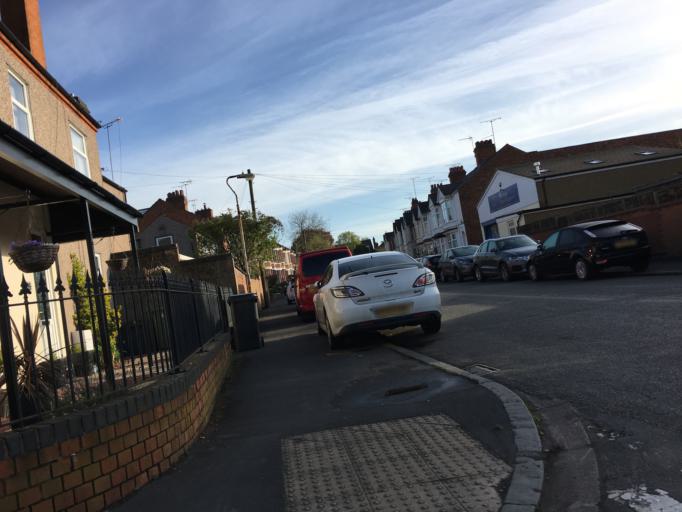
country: GB
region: England
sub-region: Warwickshire
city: Rugby
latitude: 52.3667
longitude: -1.2502
